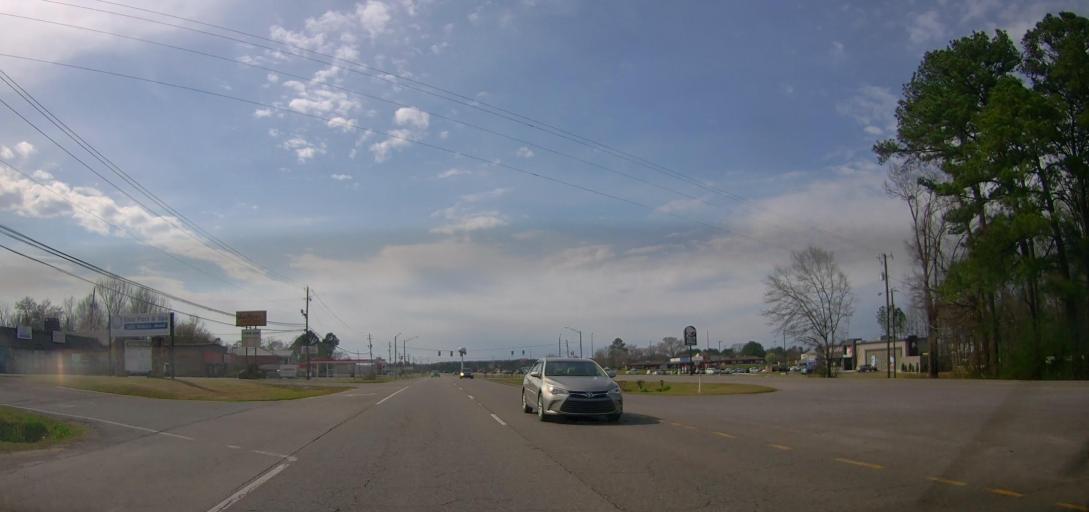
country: US
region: Alabama
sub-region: Walker County
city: Sumiton
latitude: 33.7422
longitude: -87.0406
